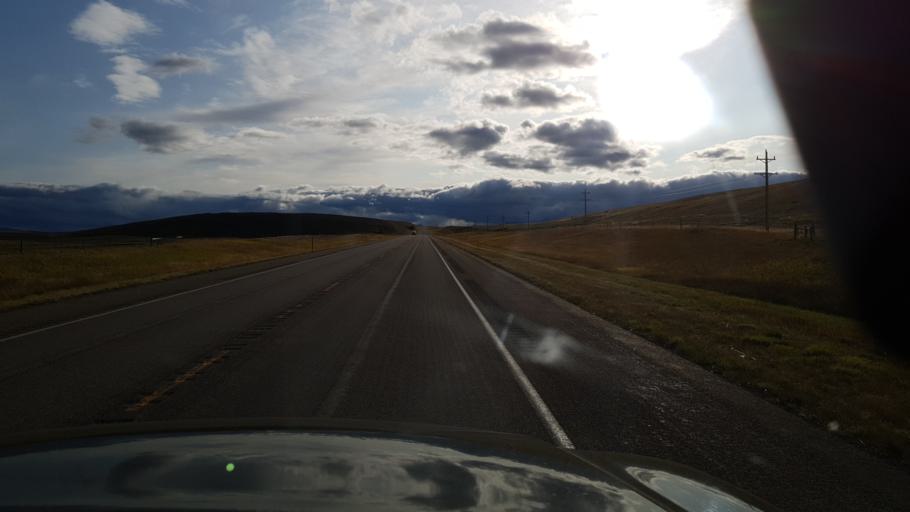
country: US
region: Montana
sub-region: Glacier County
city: South Browning
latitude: 48.5250
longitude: -113.0662
